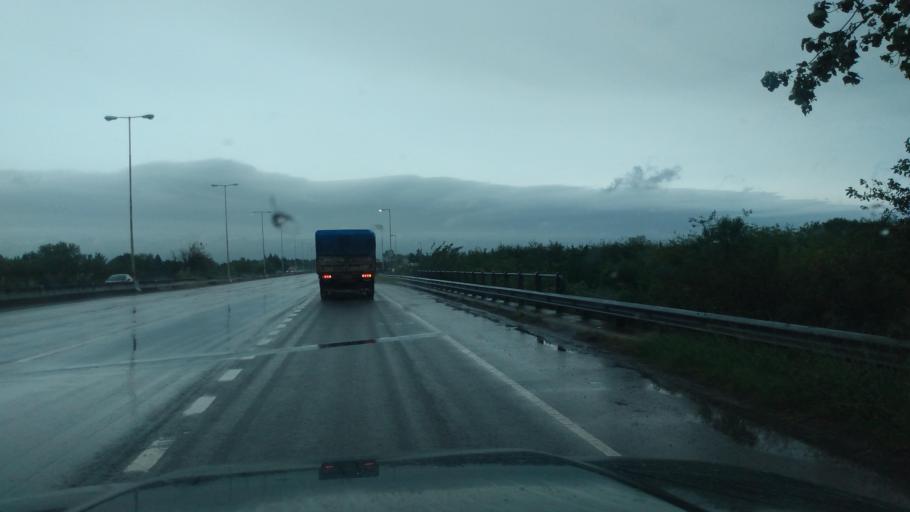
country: AR
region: Buenos Aires
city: Capilla del Senor
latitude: -34.3910
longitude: -59.0319
